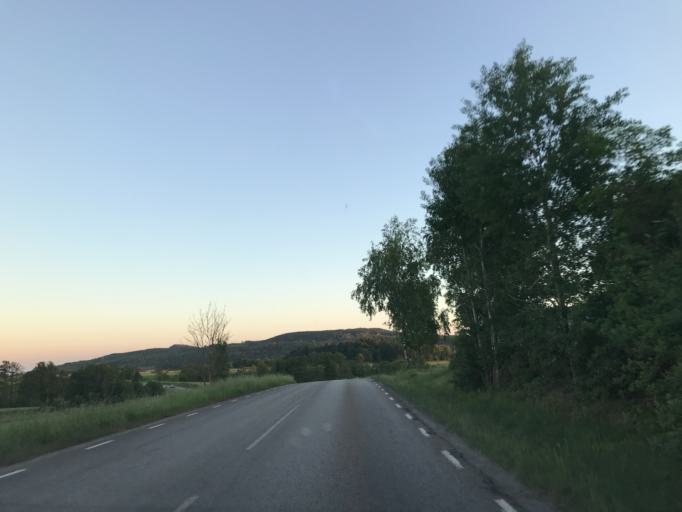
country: SE
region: Vaestra Goetaland
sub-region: Marks Kommun
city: Horred
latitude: 57.4556
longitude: 12.5083
